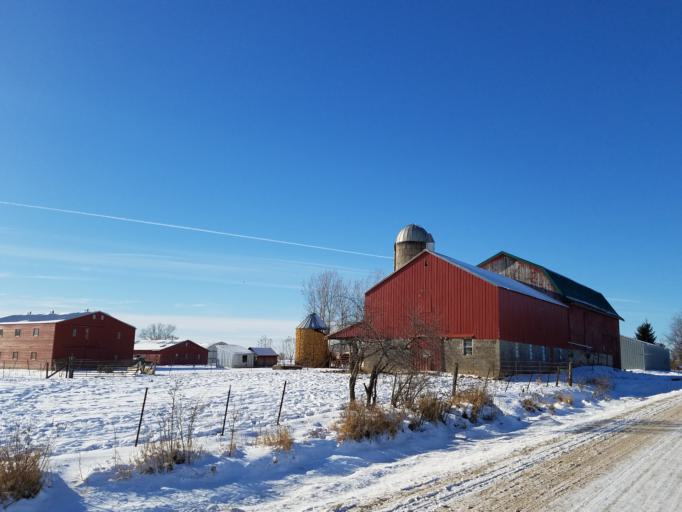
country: US
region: Wisconsin
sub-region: Clark County
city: Loyal
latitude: 44.6112
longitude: -90.4393
